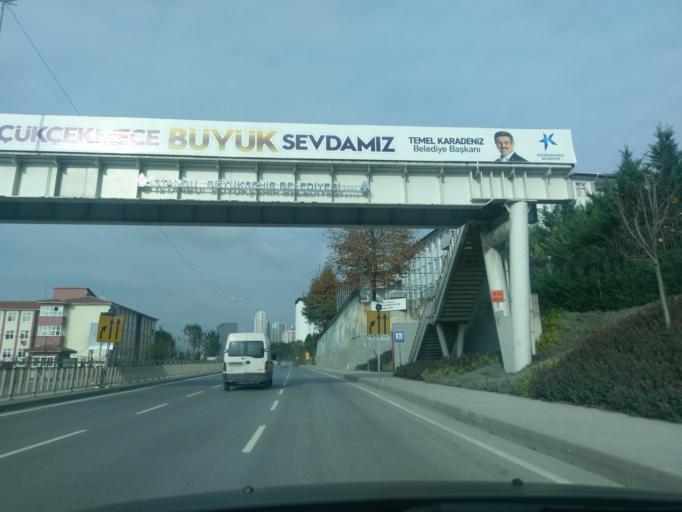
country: TR
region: Istanbul
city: Basaksehir
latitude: 41.0528
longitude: 28.7748
